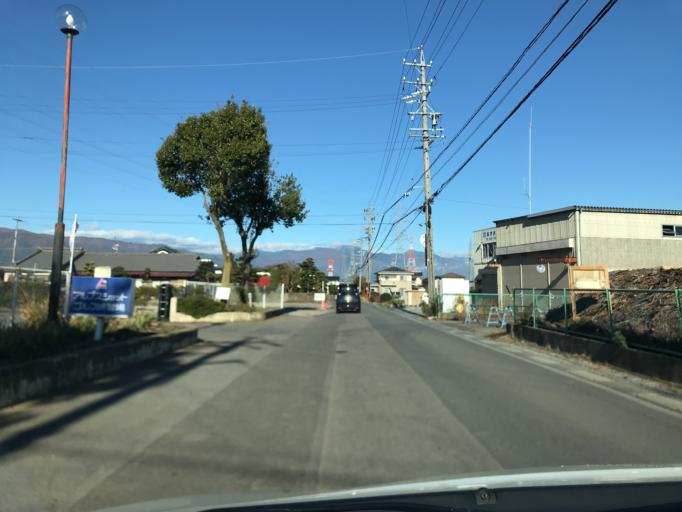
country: JP
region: Nagano
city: Shiojiri
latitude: 36.1217
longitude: 137.9414
